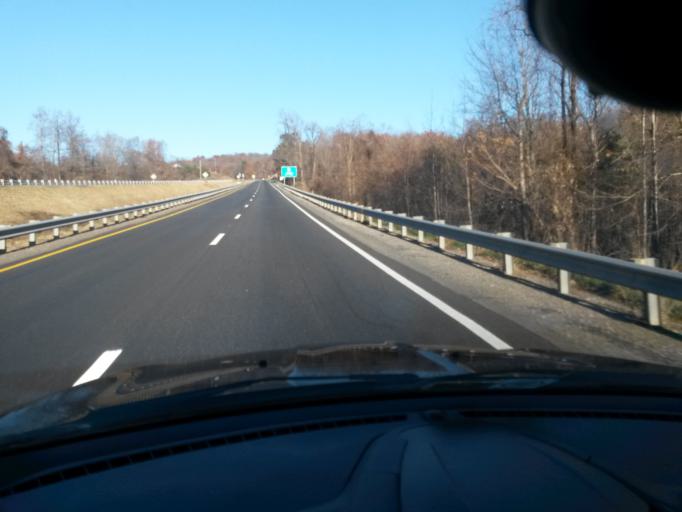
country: US
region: Virginia
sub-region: Patrick County
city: Stuart
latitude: 36.6434
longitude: -80.2482
